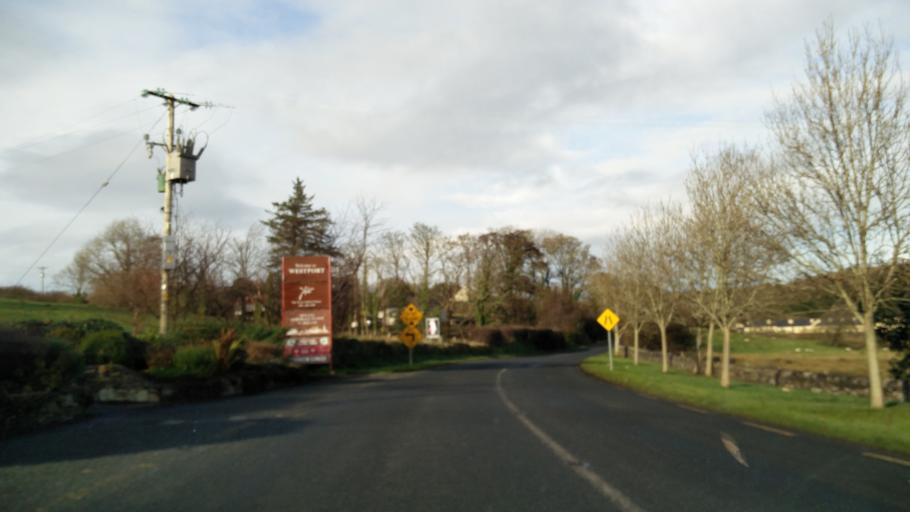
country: IE
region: Connaught
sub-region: Maigh Eo
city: Westport
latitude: 53.7900
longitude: -9.5038
